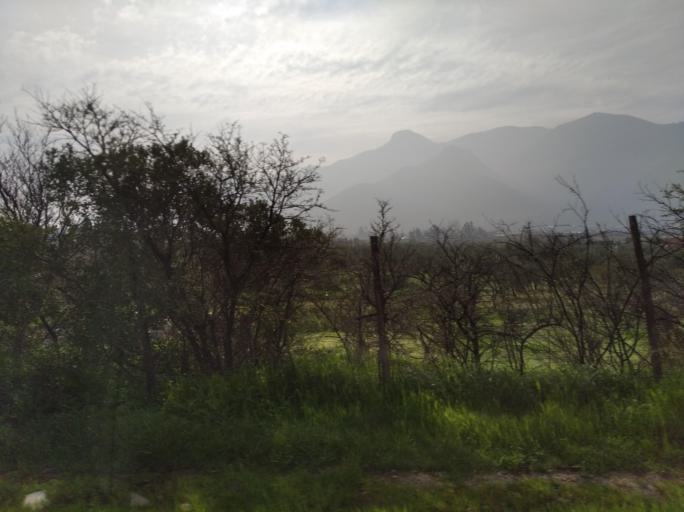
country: CL
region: Santiago Metropolitan
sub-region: Provincia de Chacabuco
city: Lampa
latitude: -33.2401
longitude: -70.9242
